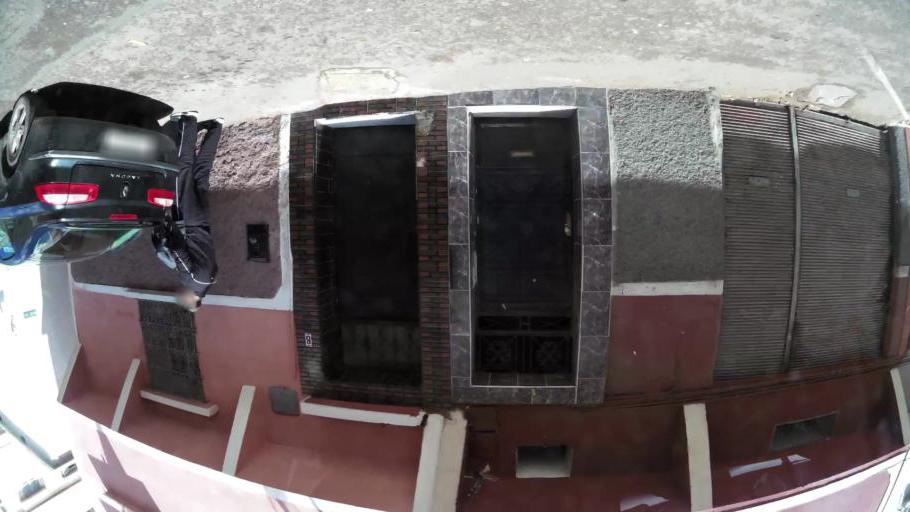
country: MA
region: Grand Casablanca
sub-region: Casablanca
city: Casablanca
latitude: 33.5581
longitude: -7.6039
